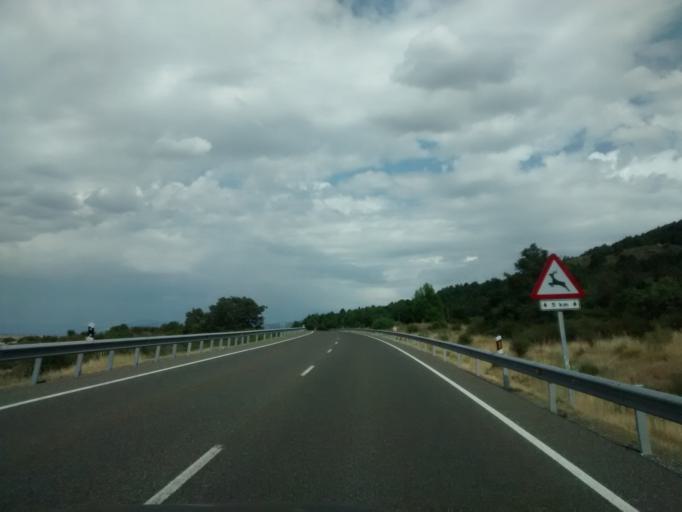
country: ES
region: Castille and Leon
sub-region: Provincia de Segovia
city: Torre Val de San Pedro
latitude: 41.0598
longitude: -3.8727
